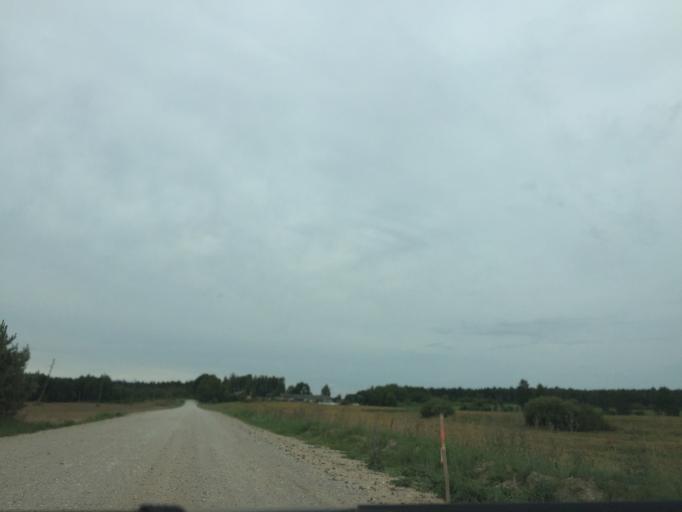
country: LV
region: Jaunpils
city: Jaunpils
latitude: 56.7277
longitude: 23.1435
